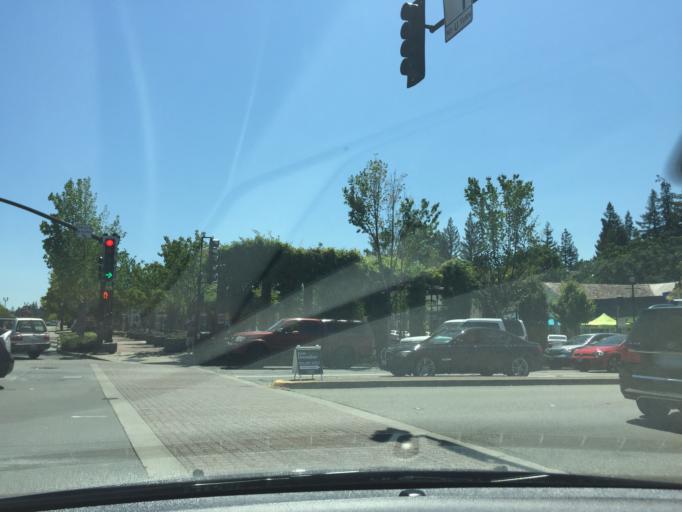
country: US
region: California
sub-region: Contra Costa County
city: Lafayette
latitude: 37.8919
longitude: -122.1189
